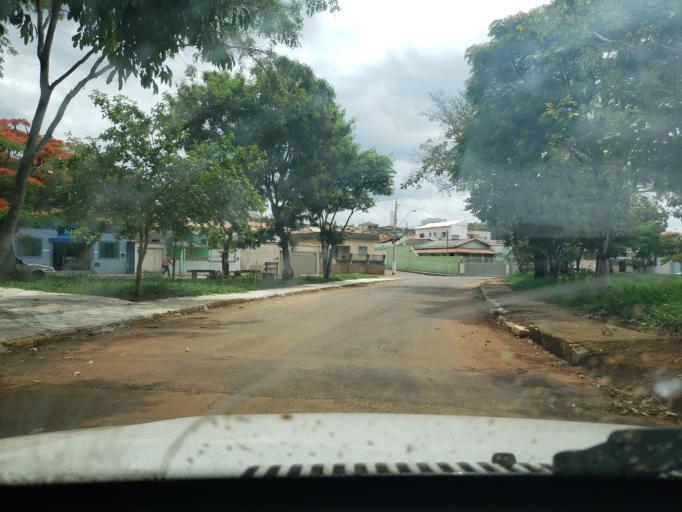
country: BR
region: Minas Gerais
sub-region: Boa Esperanca
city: Boa Esperanca
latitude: -21.0826
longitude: -45.5715
